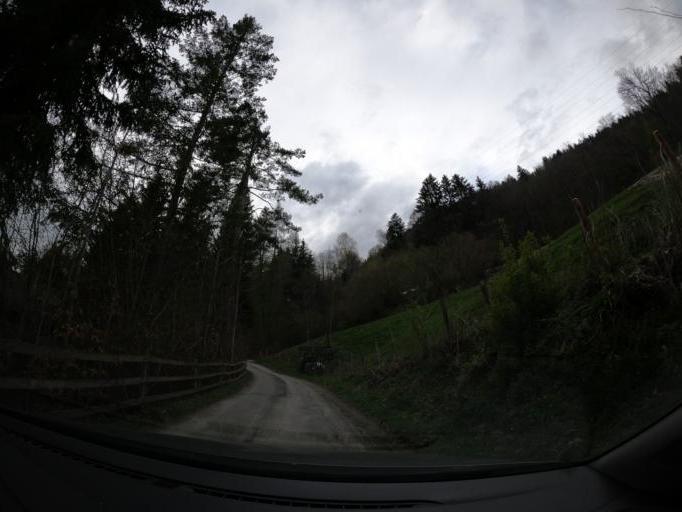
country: AT
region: Salzburg
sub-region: Politischer Bezirk Zell am See
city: Lend
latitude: 47.3023
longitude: 13.0624
